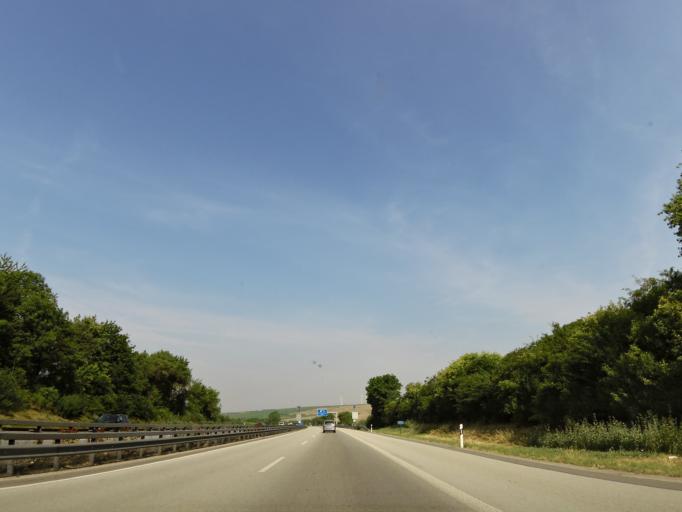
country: DE
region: Rheinland-Pfalz
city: Bermersheim
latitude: 49.6950
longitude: 8.2281
